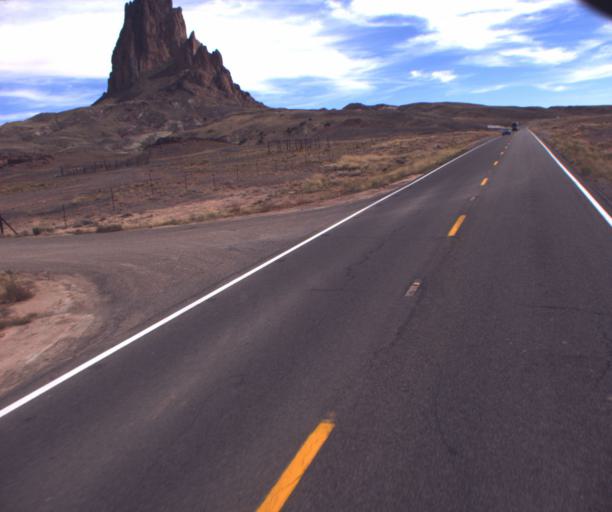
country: US
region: Arizona
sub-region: Navajo County
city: Kayenta
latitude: 36.8298
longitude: -110.2429
